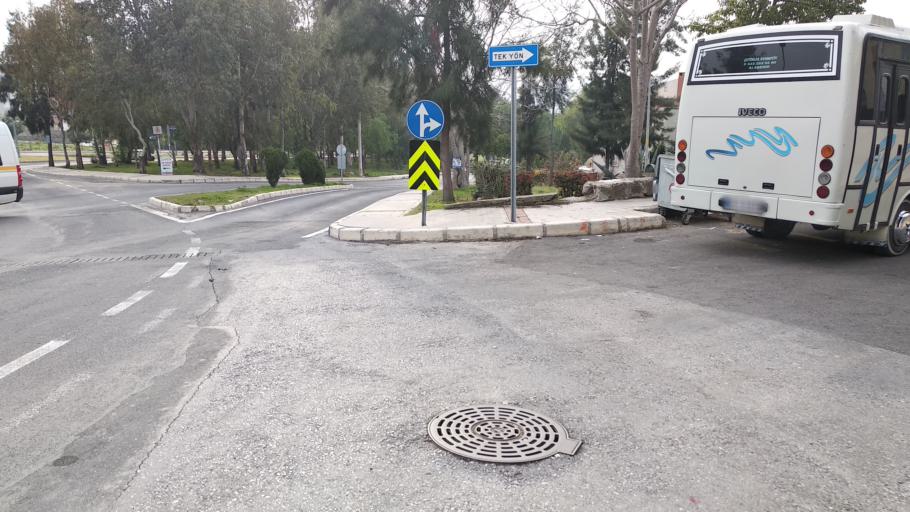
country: TR
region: Izmir
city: Karsiyaka
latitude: 38.4945
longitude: 27.0826
